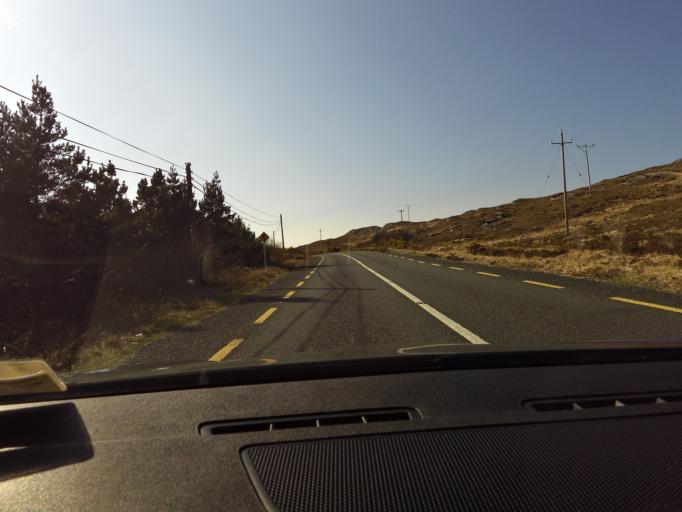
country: IE
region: Connaught
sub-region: County Galway
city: Clifden
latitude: 53.4775
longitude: -9.8913
